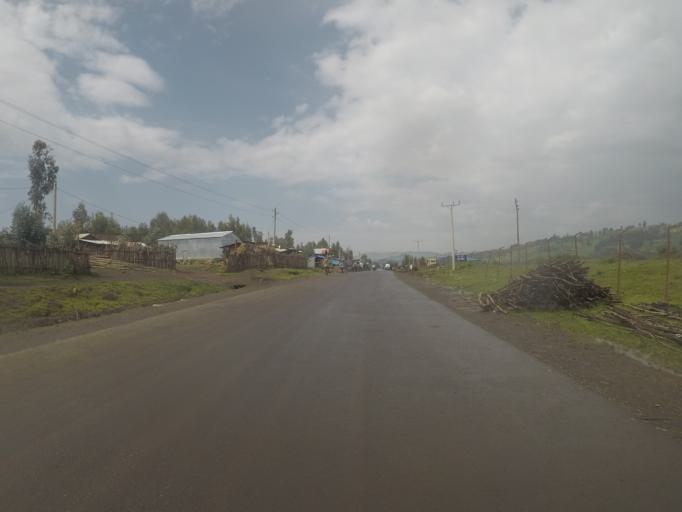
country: ET
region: Amhara
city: Debark'
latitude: 13.1246
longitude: 37.8849
